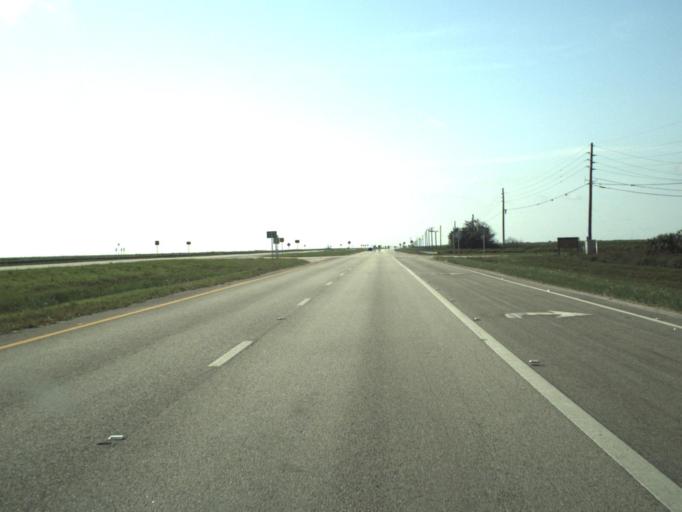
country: US
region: Florida
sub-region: Palm Beach County
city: Belle Glade Camp
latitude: 26.5531
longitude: -80.7075
